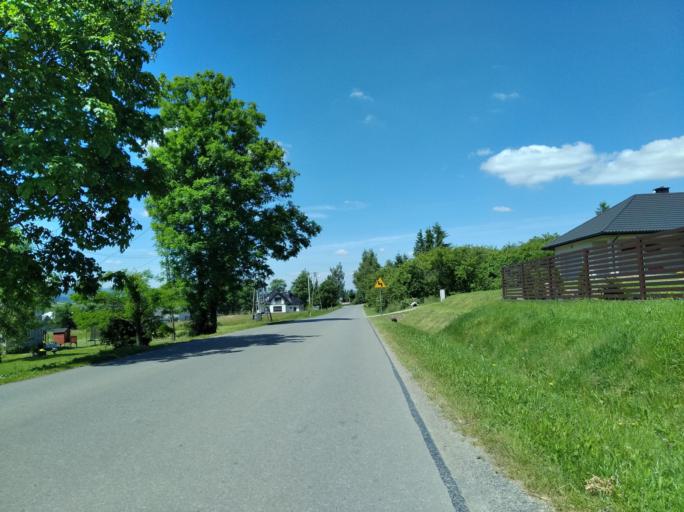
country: PL
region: Subcarpathian Voivodeship
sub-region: Powiat jasielski
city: Nowy Zmigrod
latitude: 49.6180
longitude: 21.5662
